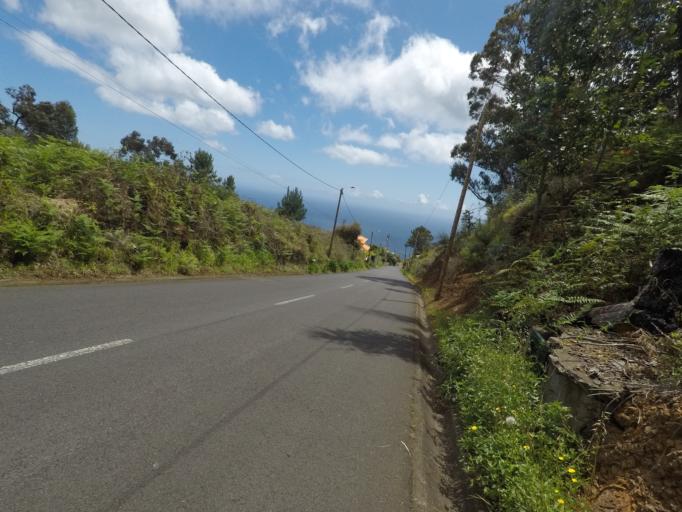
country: PT
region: Madeira
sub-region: Calheta
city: Estreito da Calheta
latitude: 32.7438
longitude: -17.1958
